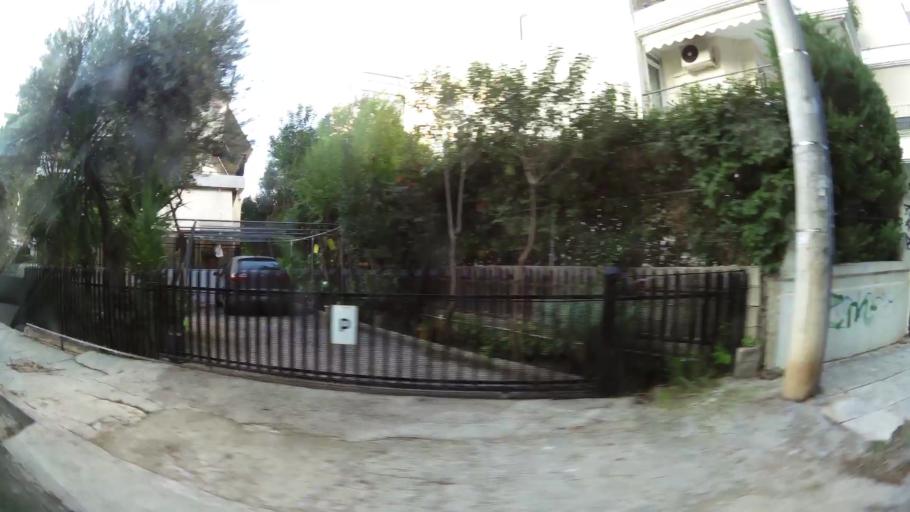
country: GR
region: Attica
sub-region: Nomarchia Athinas
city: Agia Paraskevi
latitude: 38.0158
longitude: 23.8256
